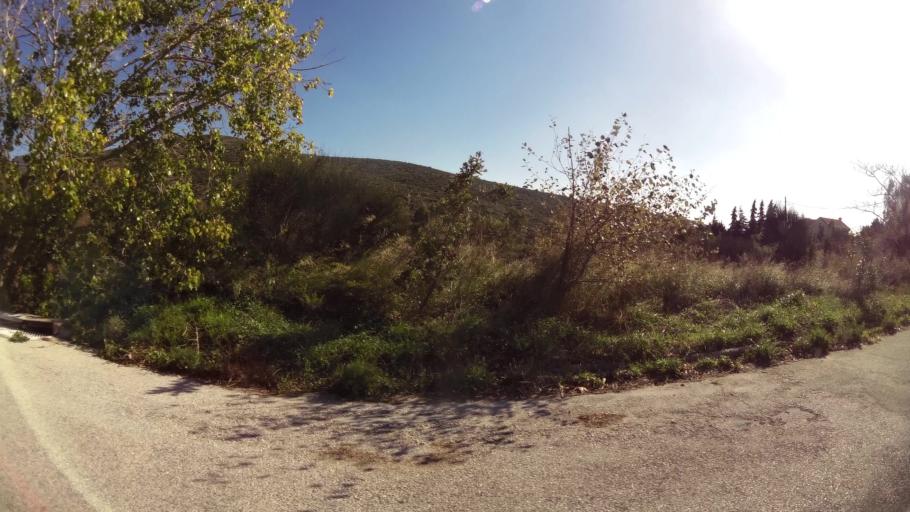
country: GR
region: Attica
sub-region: Nomarchia Anatolikis Attikis
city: Dhrafi
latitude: 38.0339
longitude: 23.9052
